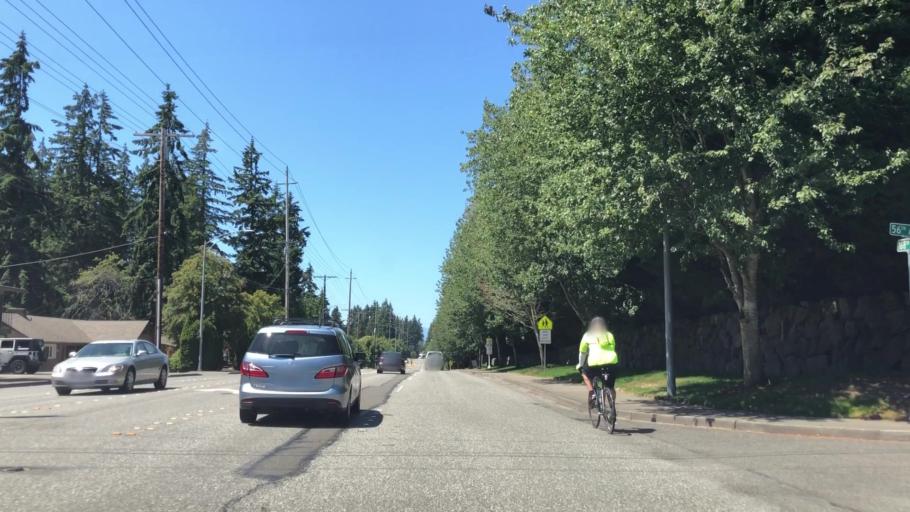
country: US
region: Washington
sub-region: Snohomish County
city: Meadowdale
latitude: 47.8467
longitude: -122.3084
